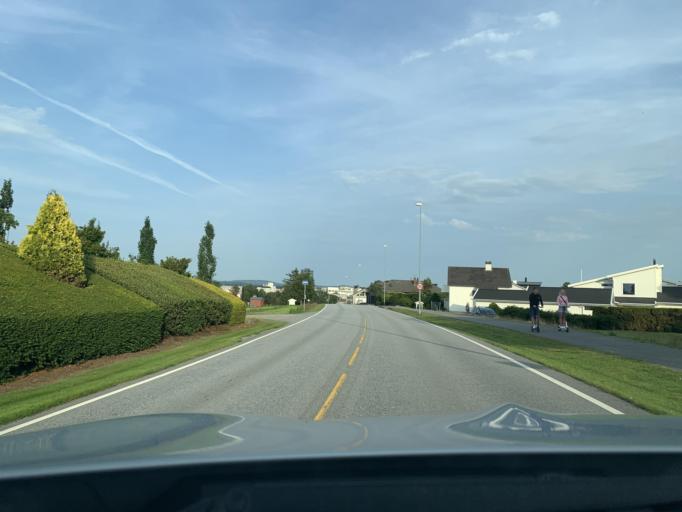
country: NO
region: Rogaland
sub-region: Time
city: Bryne
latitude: 58.7383
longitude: 5.6307
